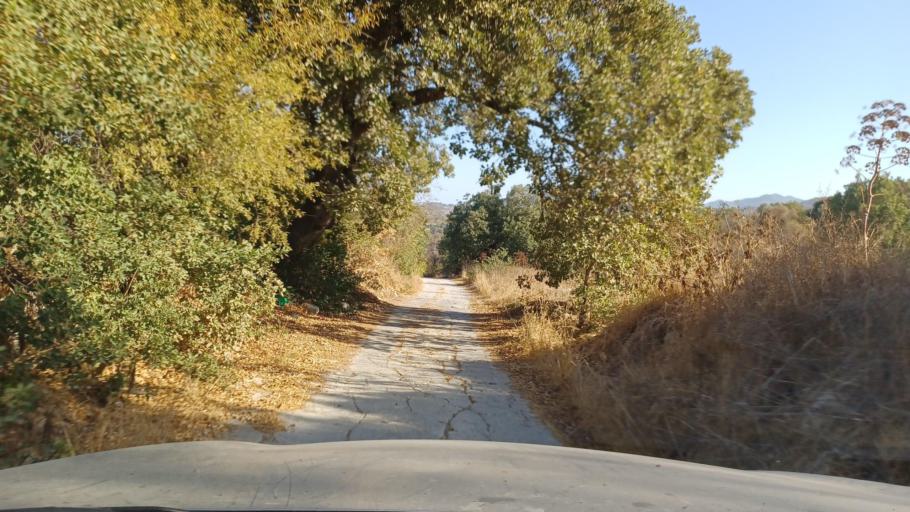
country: CY
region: Pafos
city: Polis
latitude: 34.9941
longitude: 32.4906
